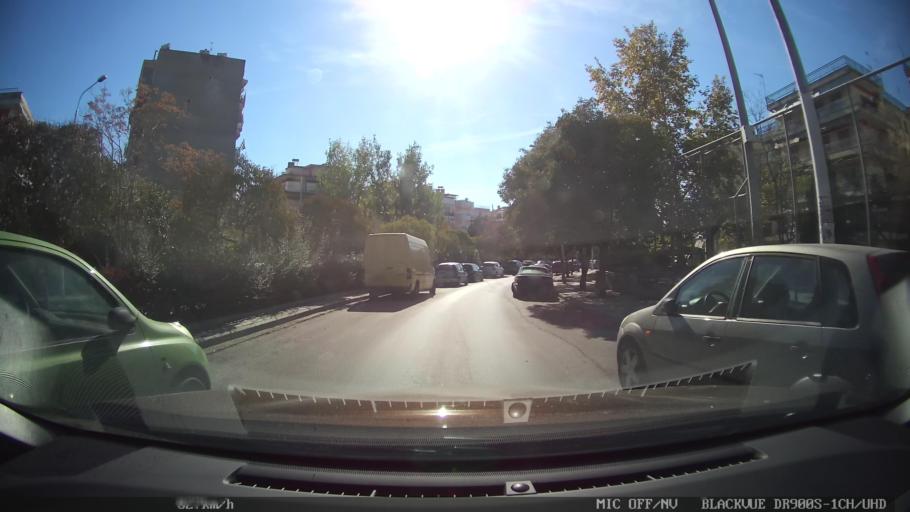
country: GR
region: Central Macedonia
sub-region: Nomos Thessalonikis
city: Triandria
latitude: 40.6117
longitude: 22.9774
